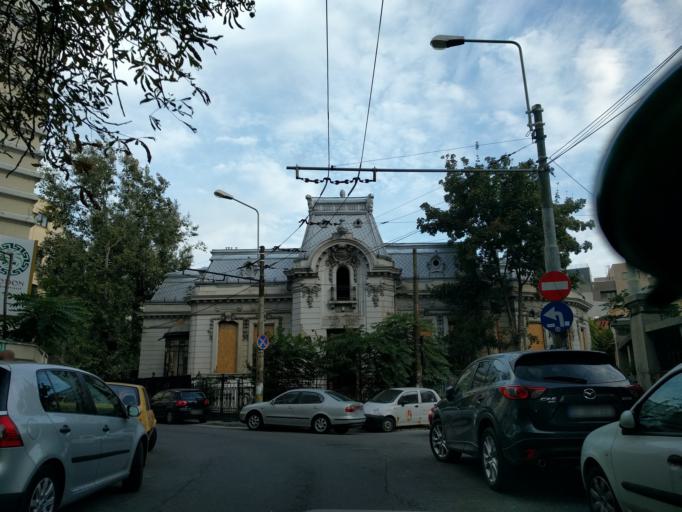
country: RO
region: Bucuresti
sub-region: Municipiul Bucuresti
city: Bucharest
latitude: 44.4375
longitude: 26.1063
